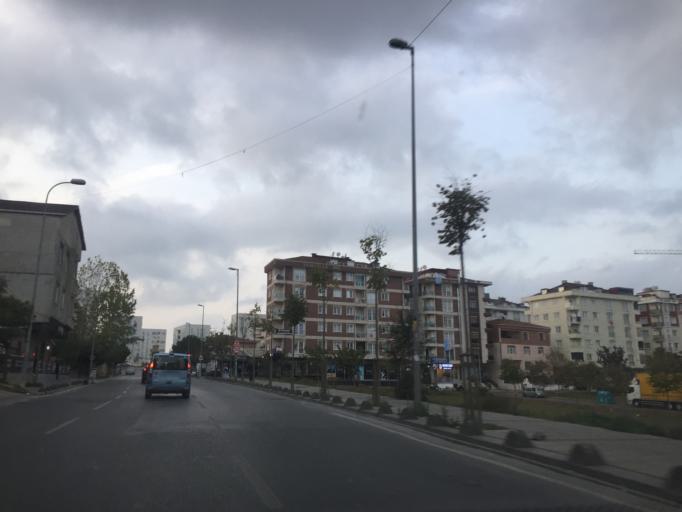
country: TR
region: Istanbul
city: Samandira
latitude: 40.9889
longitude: 29.2310
